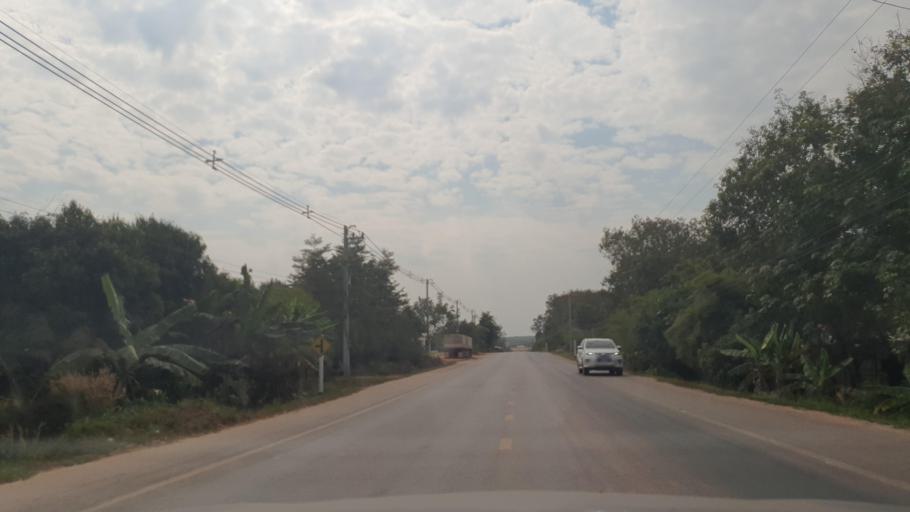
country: TH
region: Changwat Bueng Kan
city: Si Wilai
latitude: 18.2974
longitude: 103.8018
